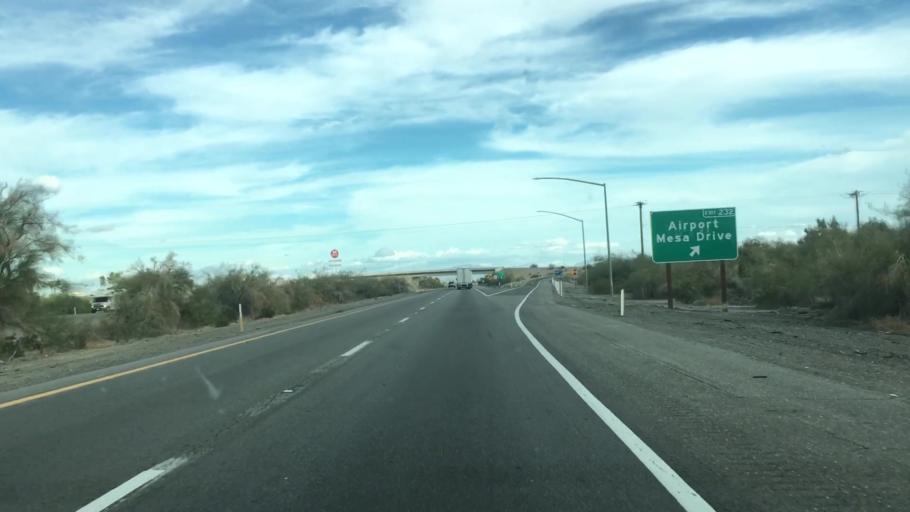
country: US
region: California
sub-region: Riverside County
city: Mesa Verde
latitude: 33.6091
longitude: -114.7317
